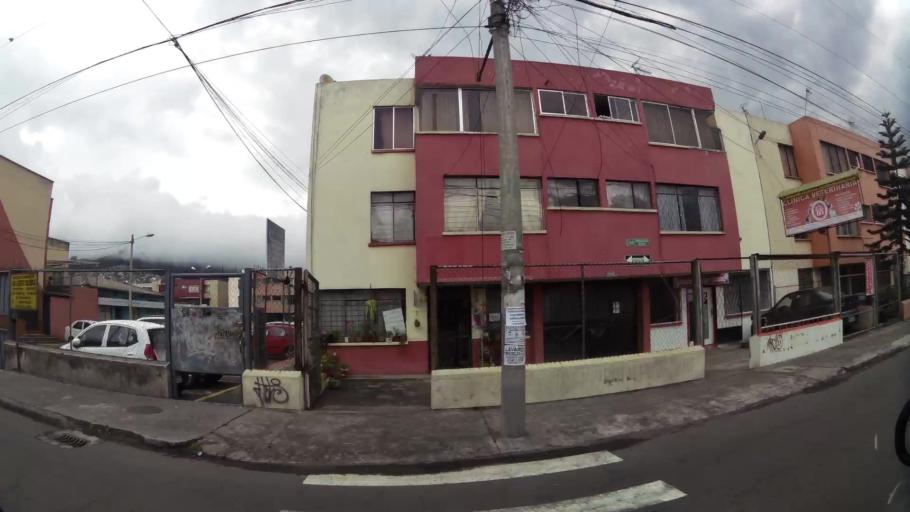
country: EC
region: Pichincha
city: Quito
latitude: -0.2667
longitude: -78.5419
